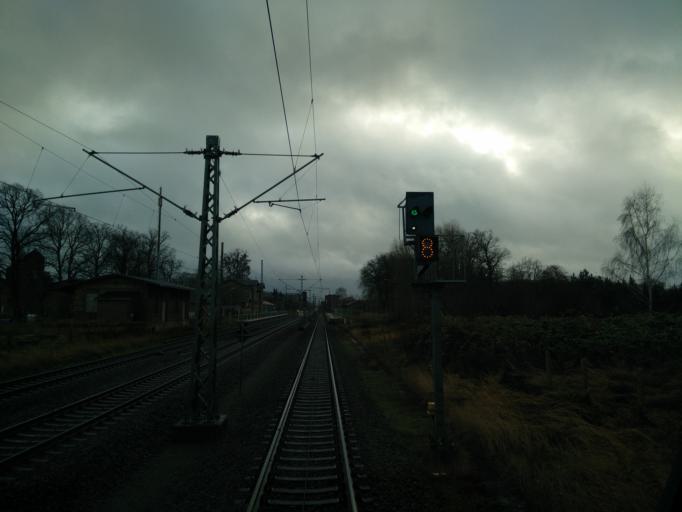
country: DE
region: Brandenburg
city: Karstadt
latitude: 53.1623
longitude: 11.7381
